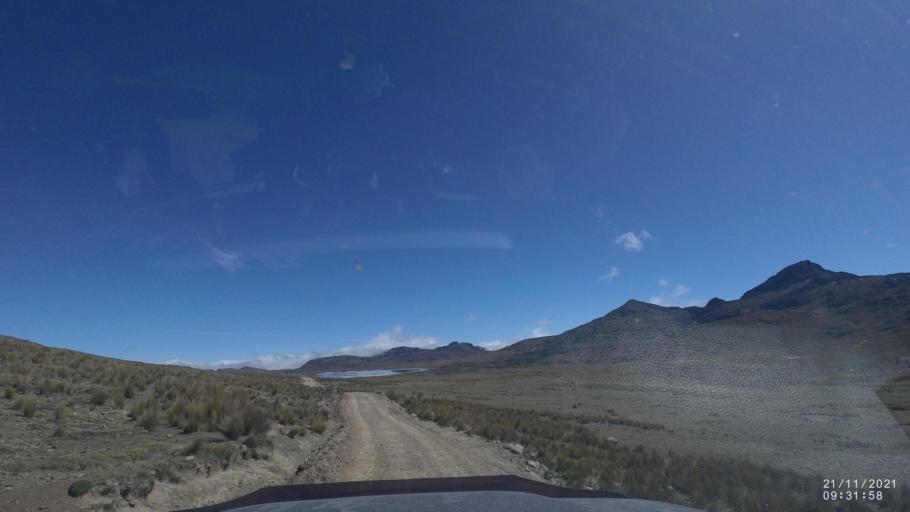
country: BO
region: Cochabamba
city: Cochabamba
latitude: -17.0696
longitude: -66.2565
